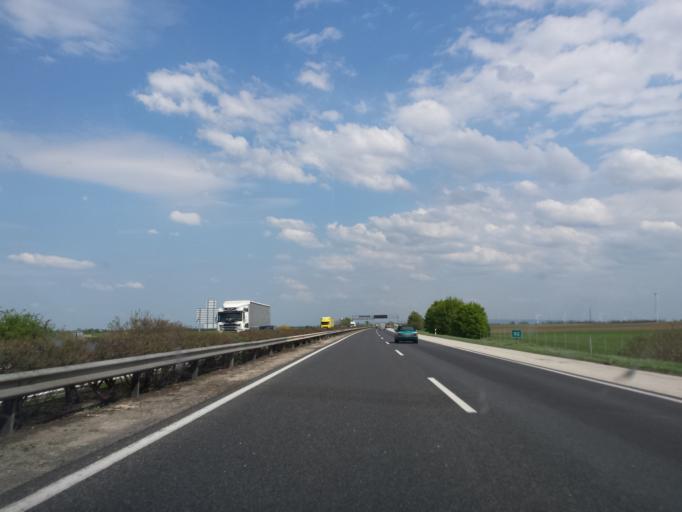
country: HU
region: Komarom-Esztergom
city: Acs
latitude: 47.6829
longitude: 17.9990
